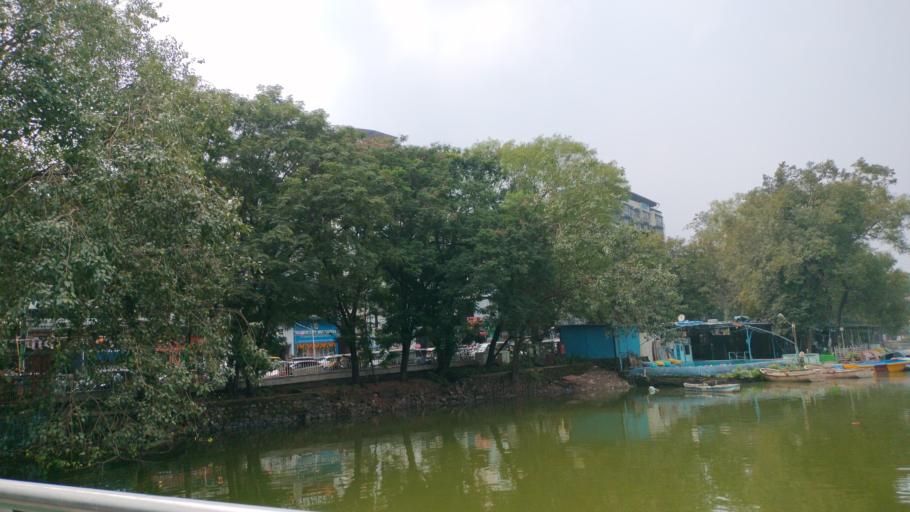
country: IN
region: Maharashtra
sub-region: Thane
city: Thane
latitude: 19.1917
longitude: 72.9763
